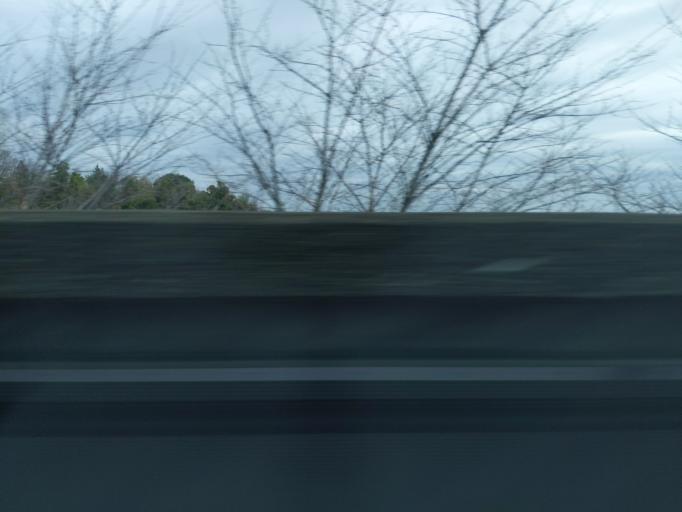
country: JP
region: Ibaraki
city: Koga
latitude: 36.1831
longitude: 139.7406
